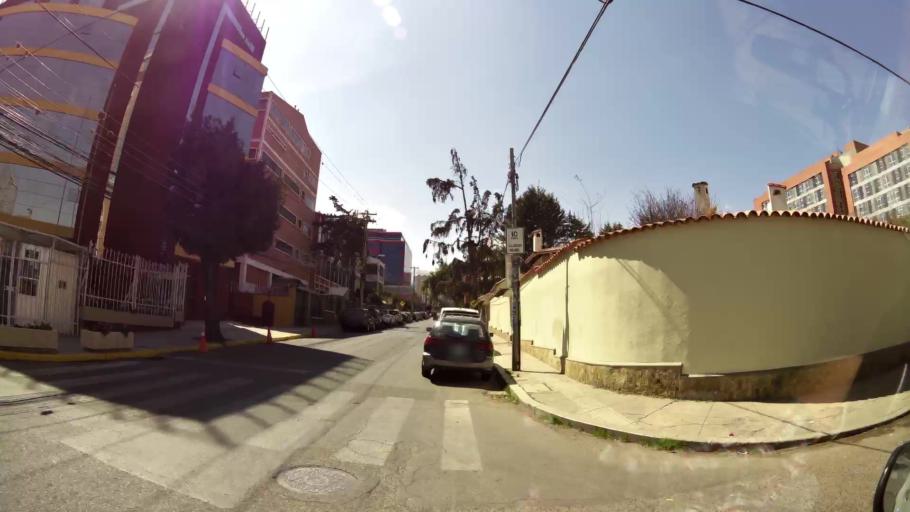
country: BO
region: La Paz
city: La Paz
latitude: -16.5405
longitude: -68.0851
